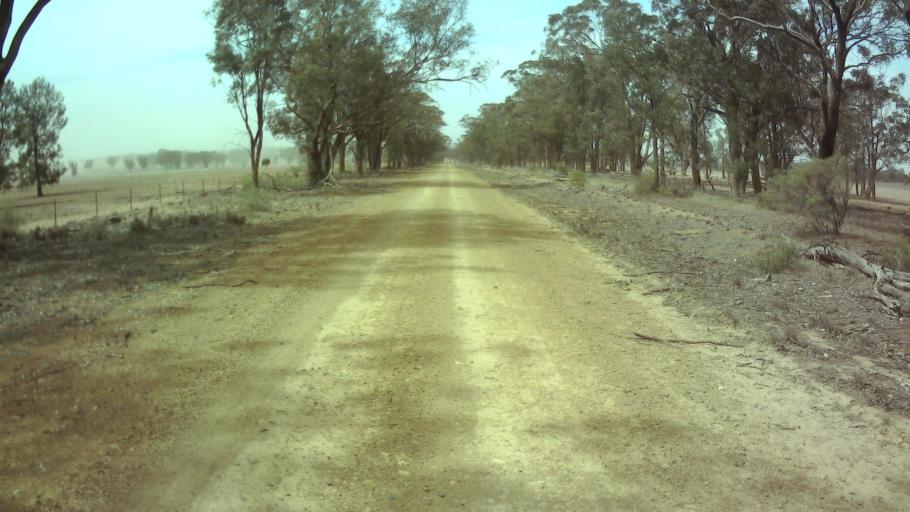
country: AU
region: New South Wales
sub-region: Weddin
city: Grenfell
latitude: -33.7351
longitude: 147.9620
